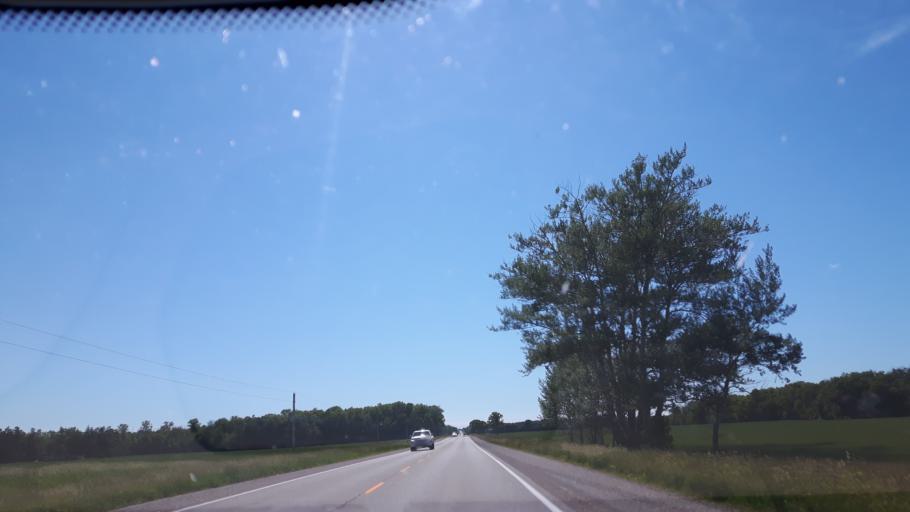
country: CA
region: Ontario
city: Bluewater
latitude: 43.4315
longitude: -81.5266
